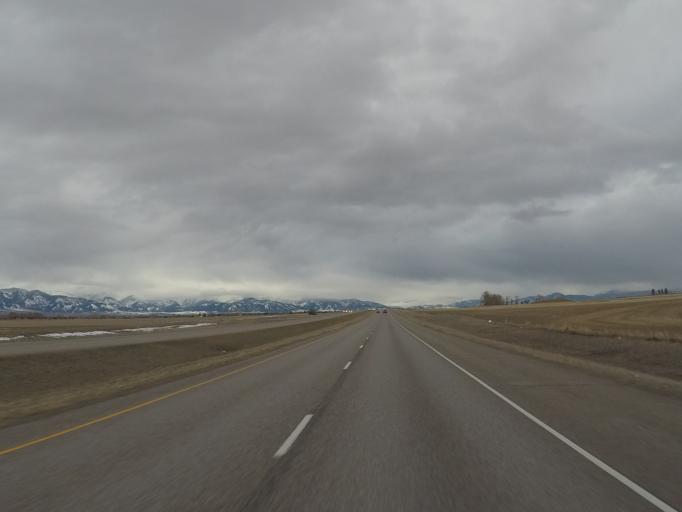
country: US
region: Montana
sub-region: Gallatin County
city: Manhattan
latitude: 45.8684
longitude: -111.3772
